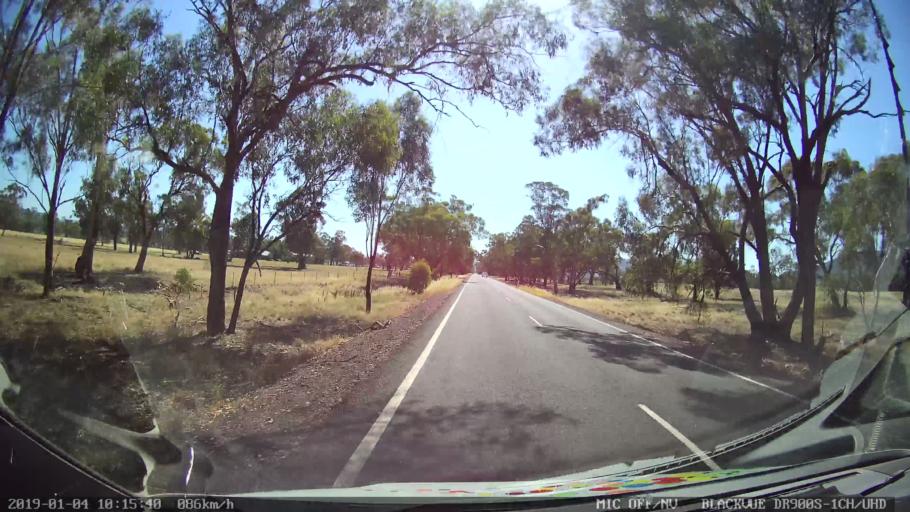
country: AU
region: New South Wales
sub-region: Cabonne
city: Canowindra
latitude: -33.3867
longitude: 148.4248
